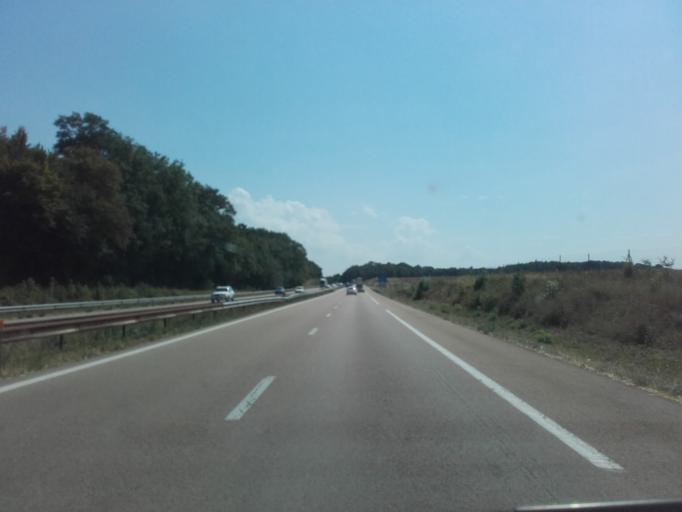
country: FR
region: Bourgogne
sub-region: Departement de l'Yonne
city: Joux-la-Ville
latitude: 47.6106
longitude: 3.9096
